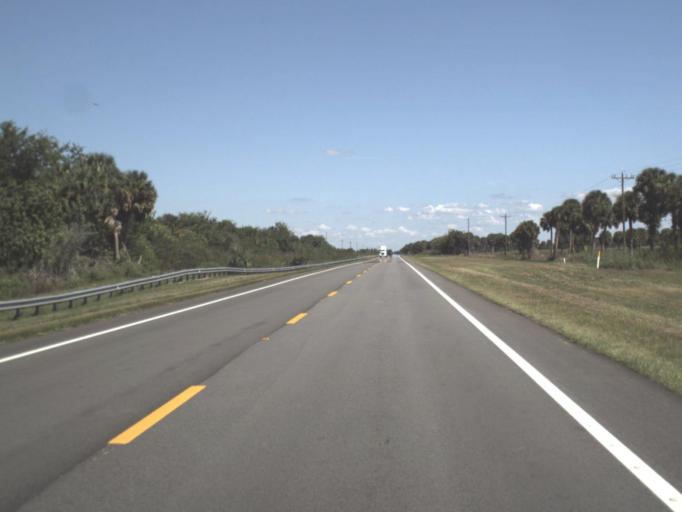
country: US
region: Florida
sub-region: Glades County
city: Buckhead Ridge
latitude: 27.0191
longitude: -81.0217
